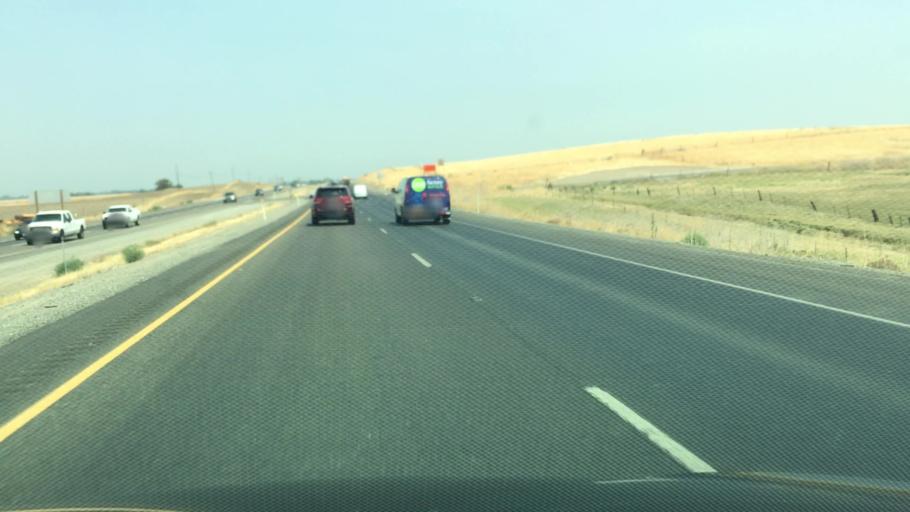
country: US
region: California
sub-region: Merced County
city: Los Banos
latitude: 37.0566
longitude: -120.9558
